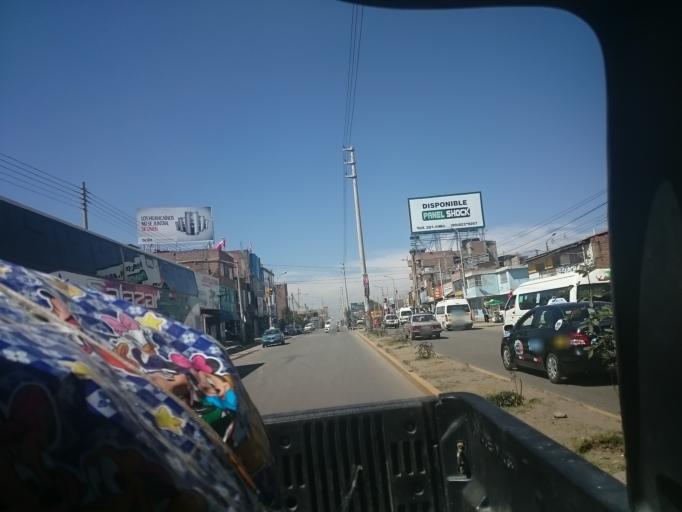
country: PE
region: Junin
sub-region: Provincia de Huancayo
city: El Tambo
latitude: -12.0453
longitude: -75.2248
